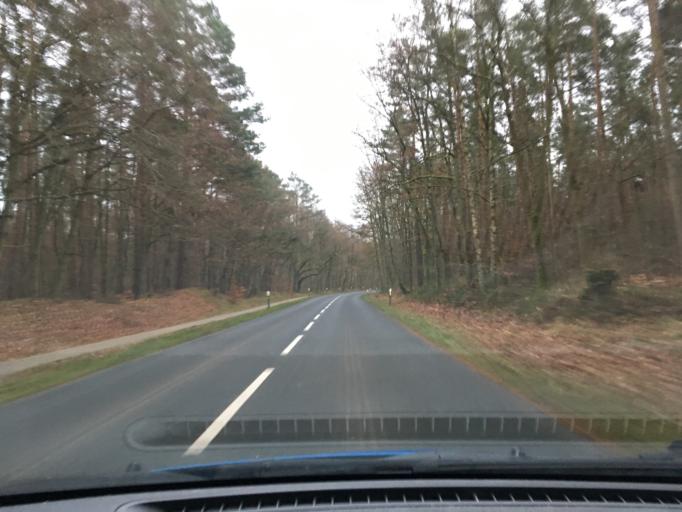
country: DE
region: Lower Saxony
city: Bleckede
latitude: 53.2775
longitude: 10.7728
